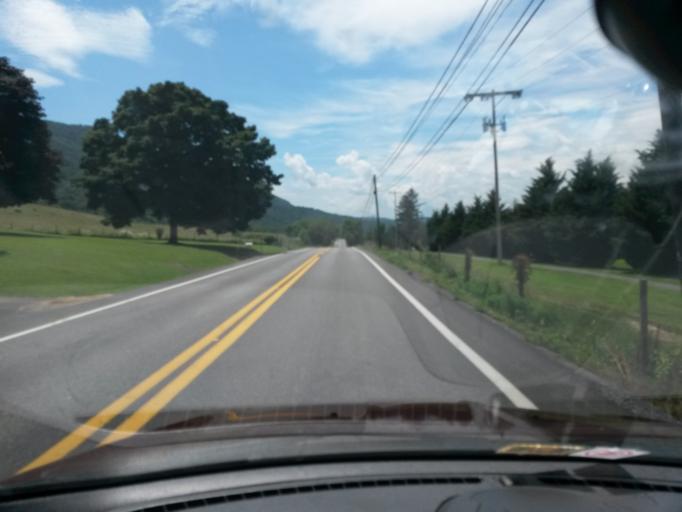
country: US
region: West Virginia
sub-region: Hardy County
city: Moorefield
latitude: 39.0051
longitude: -79.0024
